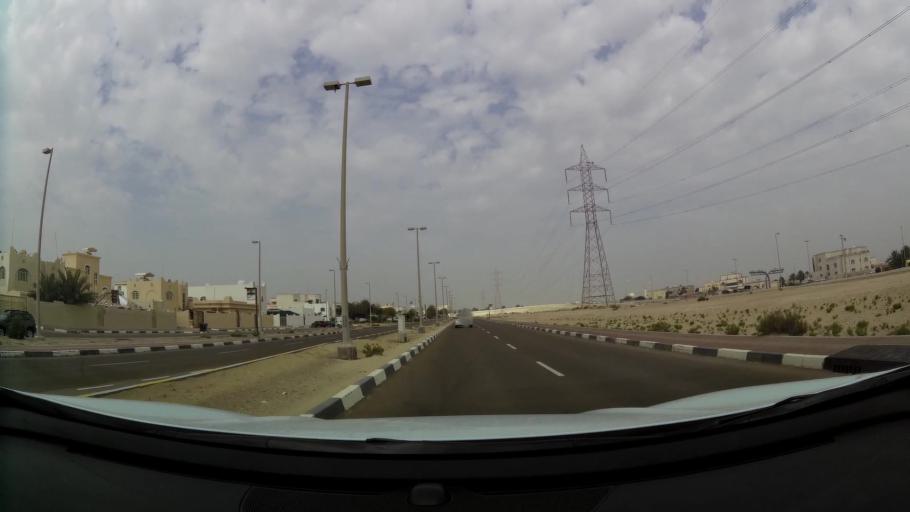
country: AE
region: Abu Dhabi
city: Abu Dhabi
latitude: 24.3221
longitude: 54.6271
